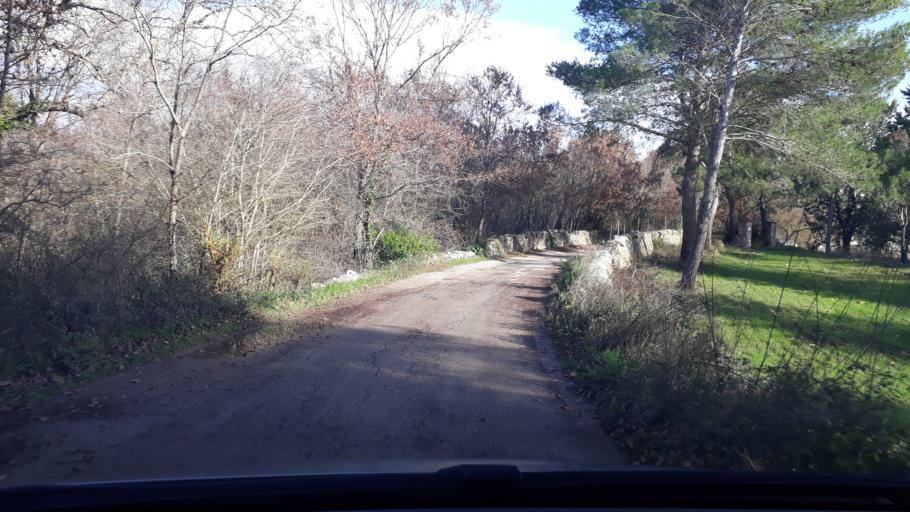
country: IT
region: Apulia
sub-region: Provincia di Brindisi
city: Cisternino
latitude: 40.6942
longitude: 17.4155
